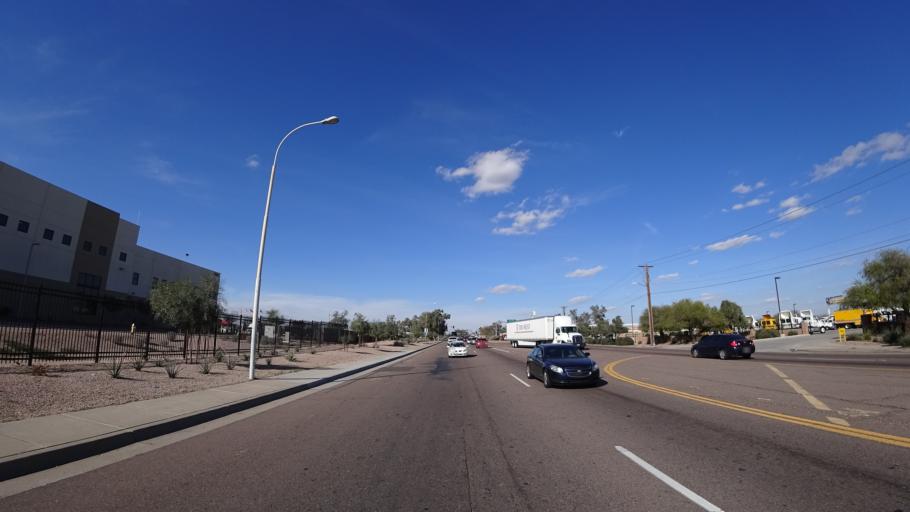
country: US
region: Arizona
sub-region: Maricopa County
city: Tolleson
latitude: 33.4601
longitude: -112.2209
